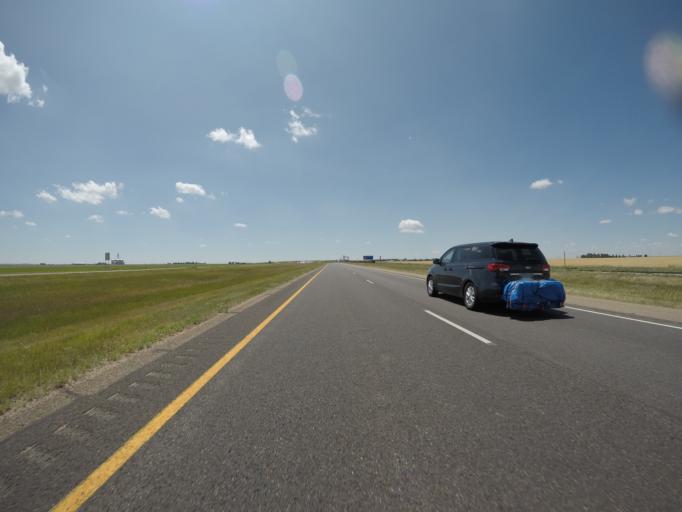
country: US
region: Colorado
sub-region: Lincoln County
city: Hugo
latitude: 39.2841
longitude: -103.2524
